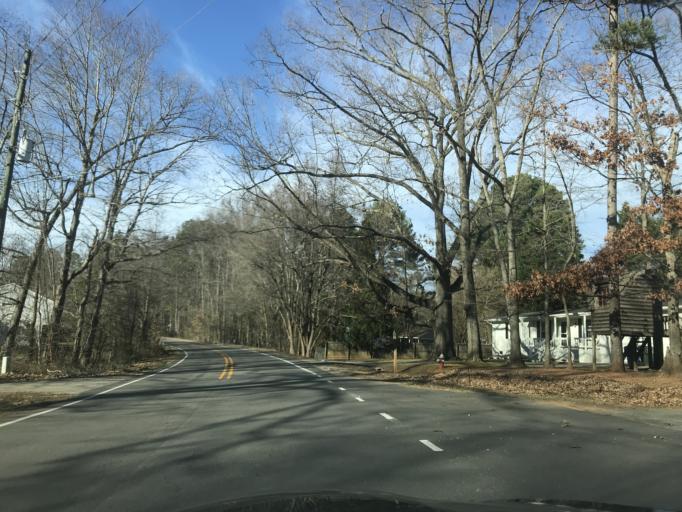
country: US
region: North Carolina
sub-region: Wake County
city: Cary
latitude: 35.7813
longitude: -78.7369
